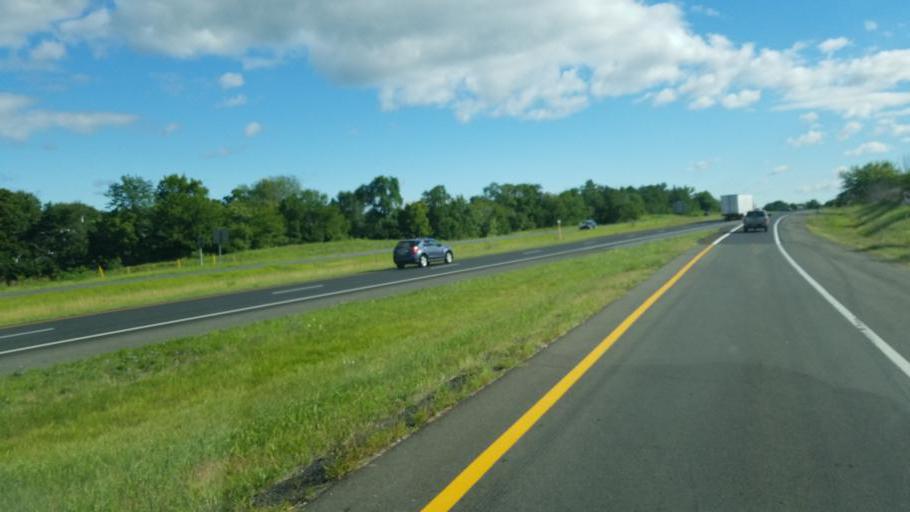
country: US
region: Virginia
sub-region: Frederick County
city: Stephens City
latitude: 39.0827
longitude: -78.2138
